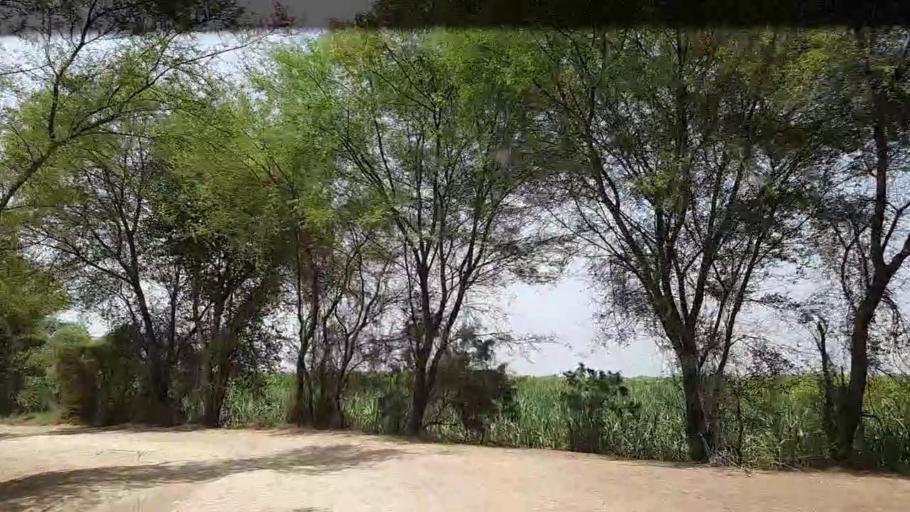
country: PK
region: Sindh
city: Ghotki
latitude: 28.0821
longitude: 69.3185
